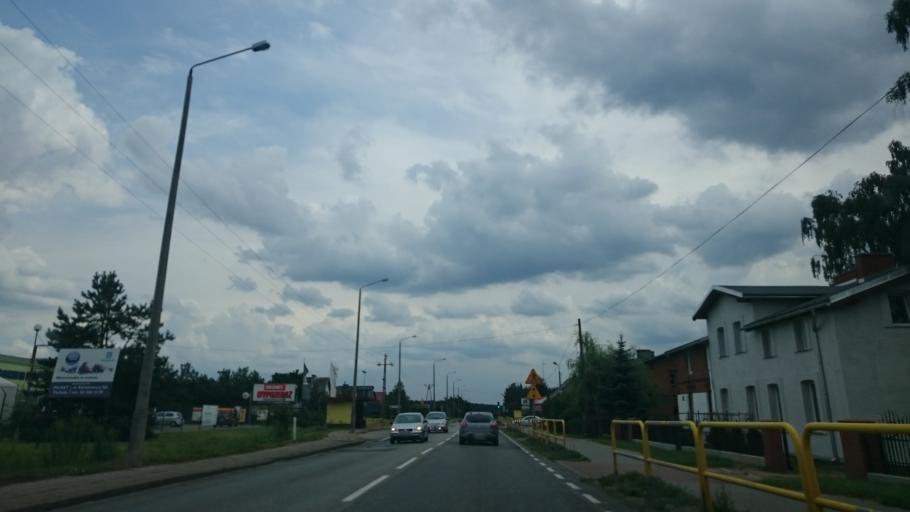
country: PL
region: Kujawsko-Pomorskie
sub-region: Powiat tucholski
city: Tuchola
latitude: 53.5701
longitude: 17.8897
